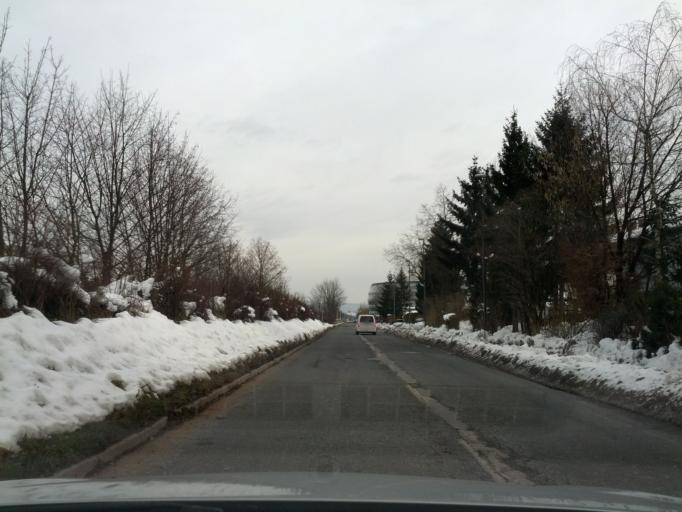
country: SI
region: Ljubljana
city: Ljubljana
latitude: 46.0837
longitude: 14.5079
